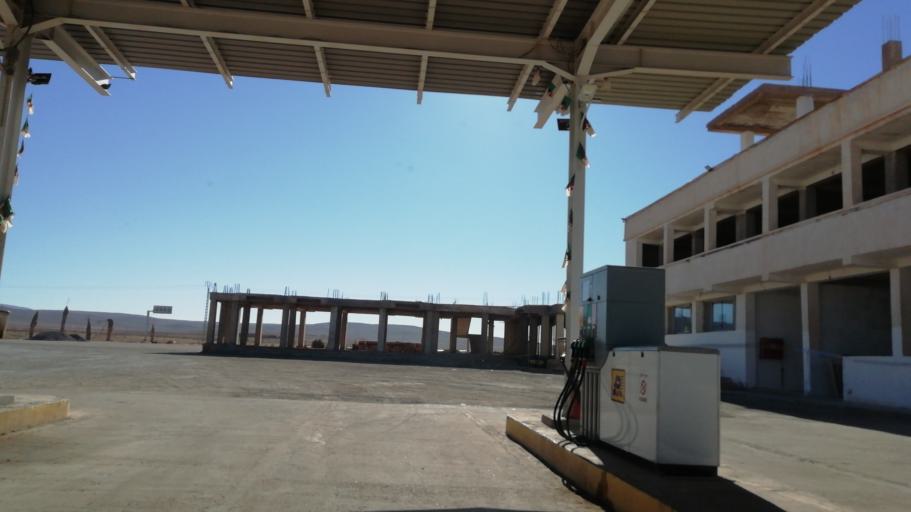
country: DZ
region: El Bayadh
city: El Bayadh
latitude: 33.6554
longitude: 0.9068
